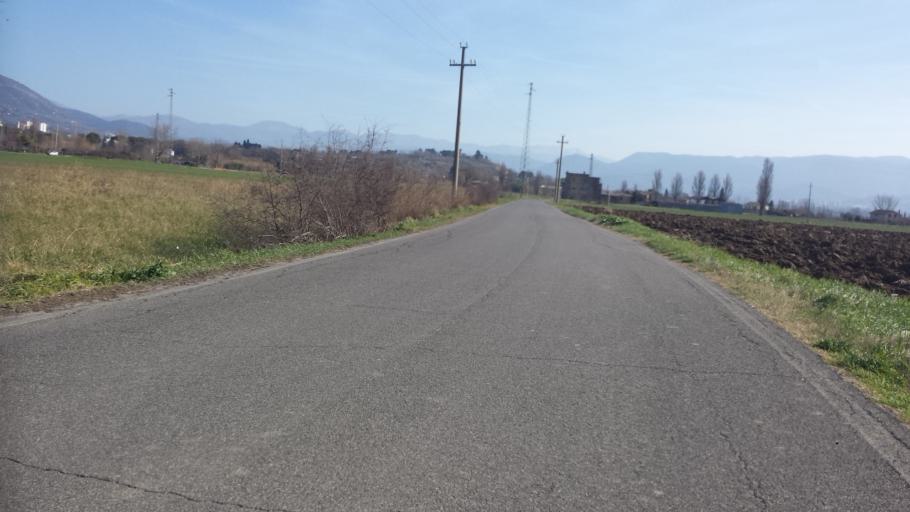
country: IT
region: Umbria
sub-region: Provincia di Terni
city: San Gemini
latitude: 42.5799
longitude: 12.5834
